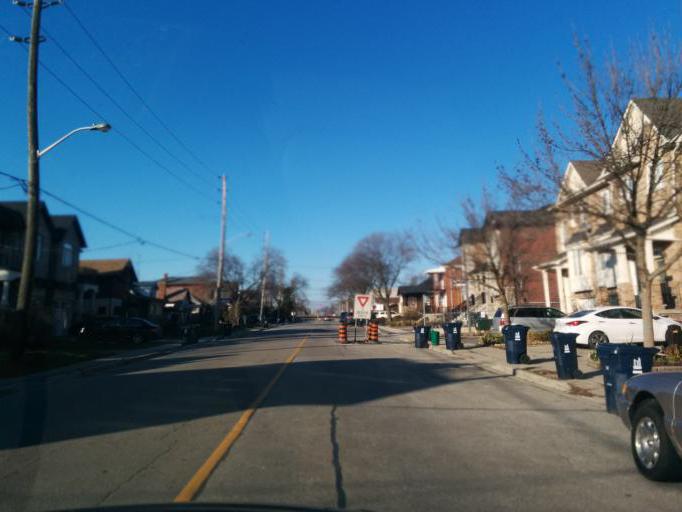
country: CA
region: Ontario
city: Etobicoke
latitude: 43.5963
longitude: -79.5301
